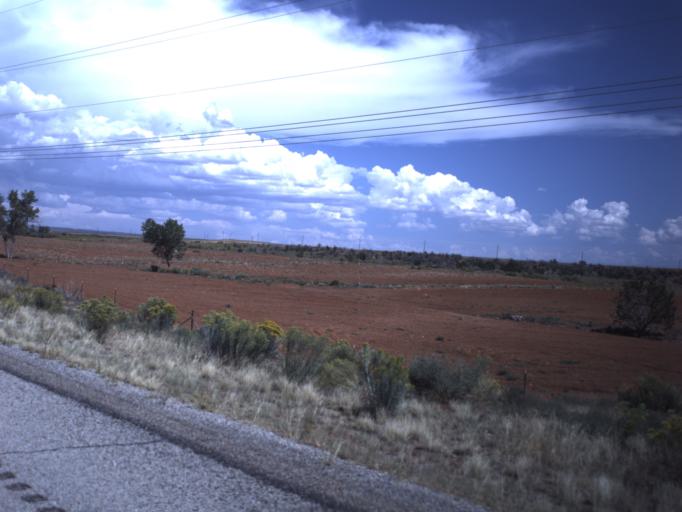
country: US
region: Utah
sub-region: San Juan County
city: Blanding
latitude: 37.5542
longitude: -109.4896
